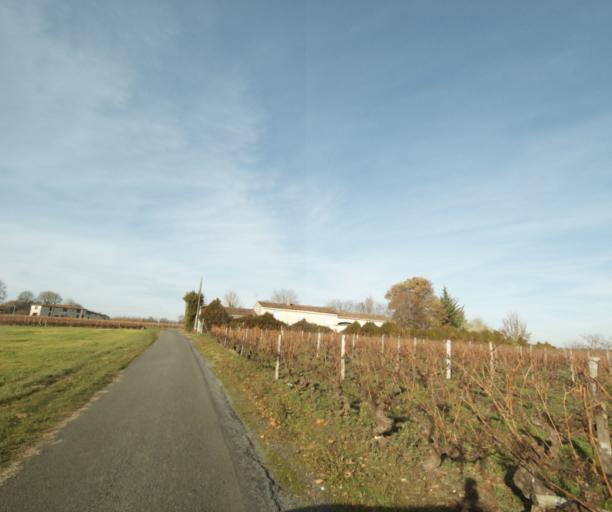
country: FR
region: Poitou-Charentes
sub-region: Departement de la Charente-Maritime
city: Chaniers
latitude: 45.7385
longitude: -0.5127
